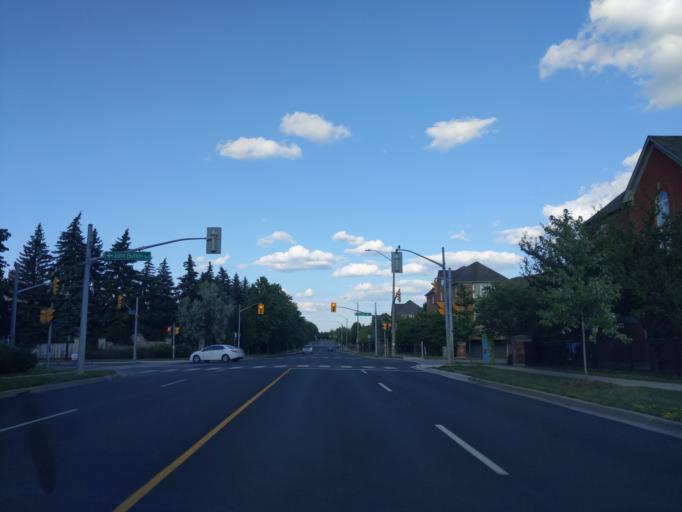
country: CA
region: Ontario
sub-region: York
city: Richmond Hill
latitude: 43.8583
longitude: -79.3533
